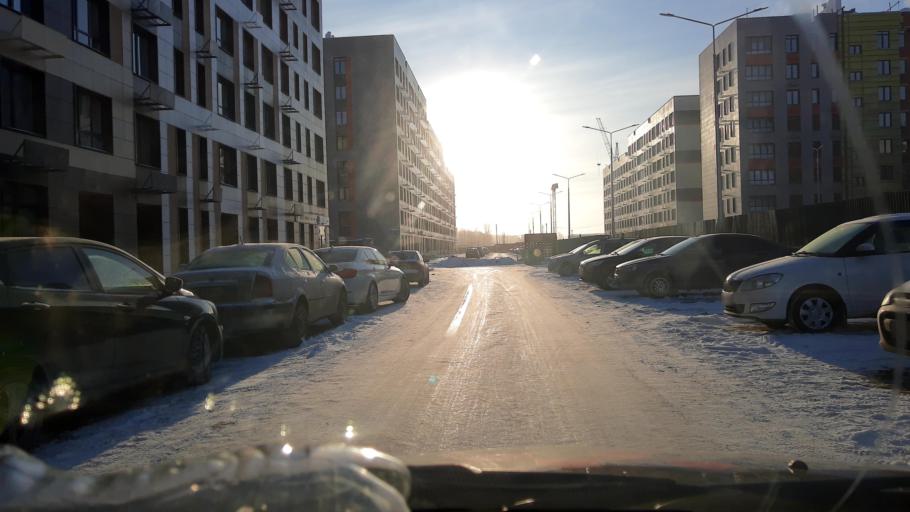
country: RU
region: Bashkortostan
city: Ufa
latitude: 54.6750
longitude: 55.9181
